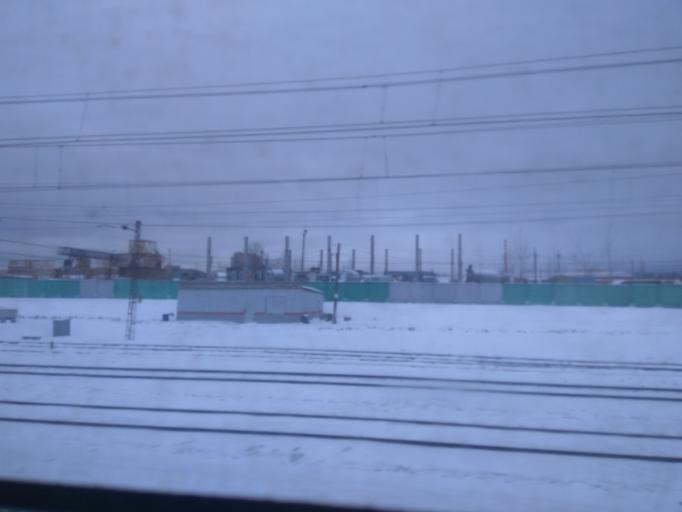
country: RU
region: Moskovskaya
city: Shcherbinka
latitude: 55.4773
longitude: 37.5546
